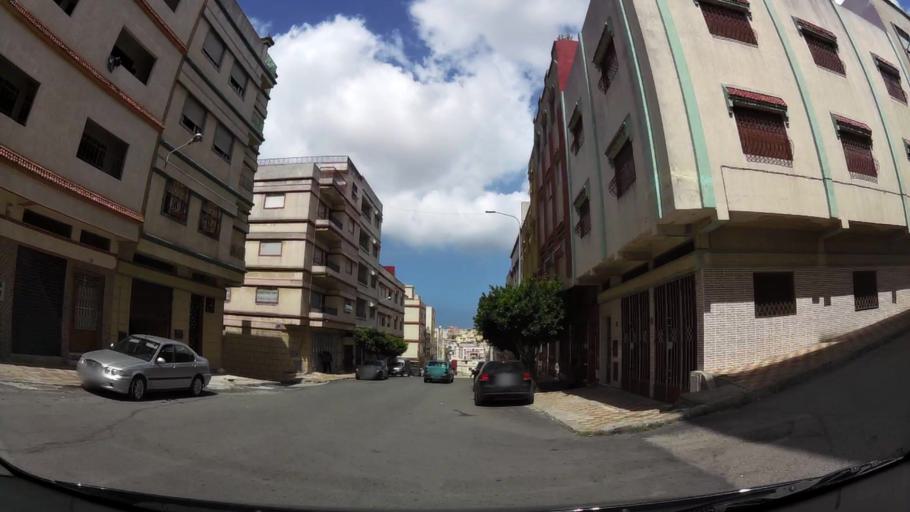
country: MA
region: Tanger-Tetouan
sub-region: Tanger-Assilah
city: Tangier
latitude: 35.7562
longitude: -5.8280
